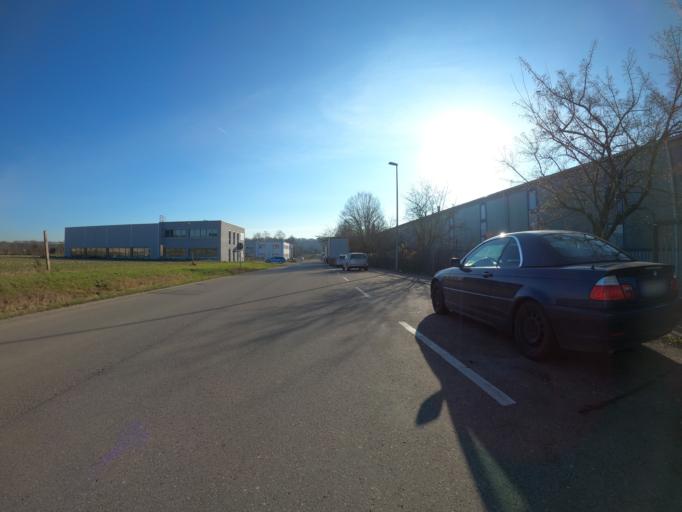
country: DE
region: Baden-Wuerttemberg
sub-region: Regierungsbezirk Stuttgart
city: Schlierbach
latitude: 48.6783
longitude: 9.5359
